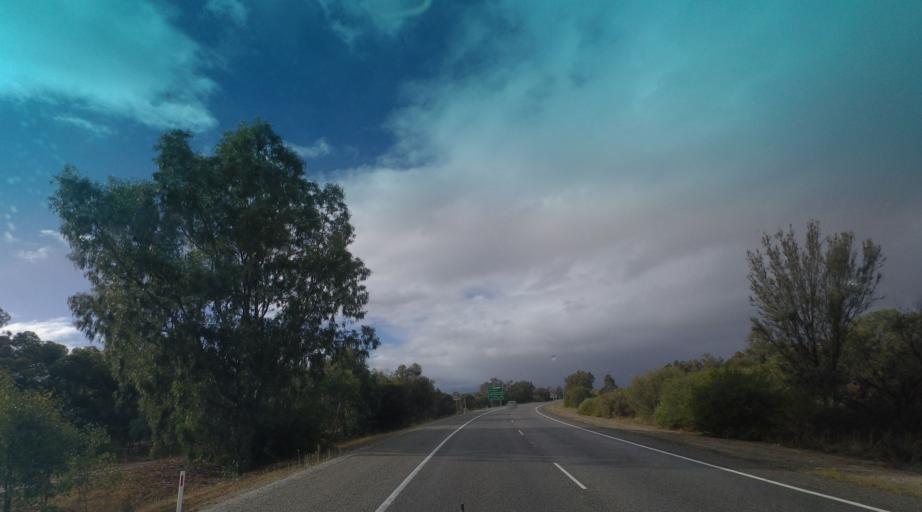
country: AU
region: Western Australia
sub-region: Serpentine-Jarrahdale
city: Oakford
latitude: -32.2040
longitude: 115.9682
